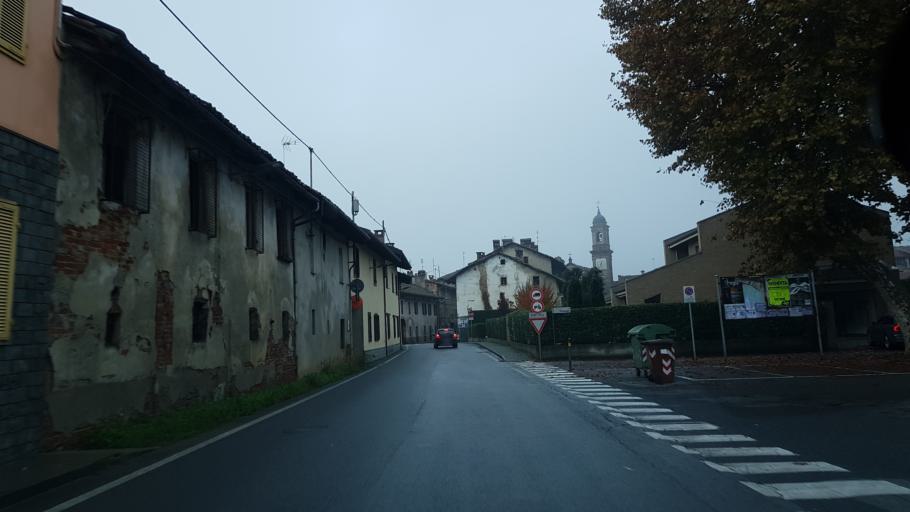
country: IT
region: Piedmont
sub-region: Provincia di Cuneo
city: Vottignasco
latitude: 44.5568
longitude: 7.6240
